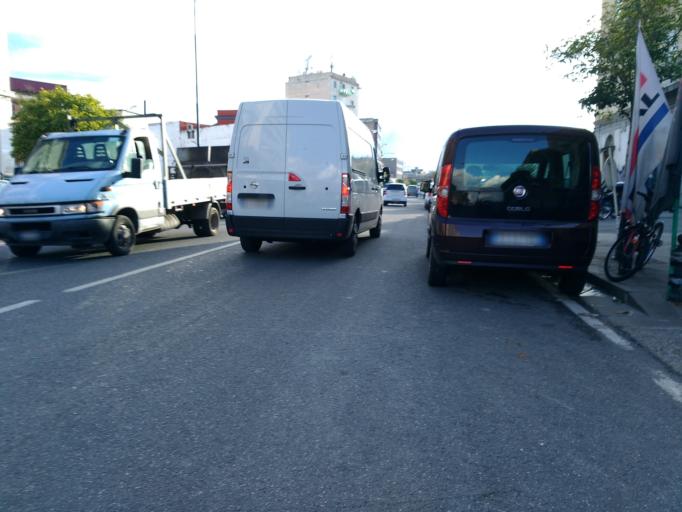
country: IT
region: Campania
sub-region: Provincia di Napoli
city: Napoli
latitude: 40.8489
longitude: 14.2888
